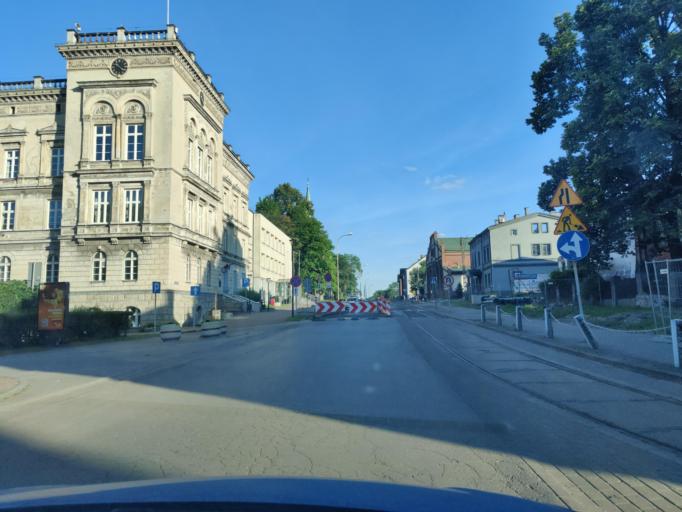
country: PL
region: Silesian Voivodeship
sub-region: Myslowice
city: Myslowice
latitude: 50.2412
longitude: 19.1410
